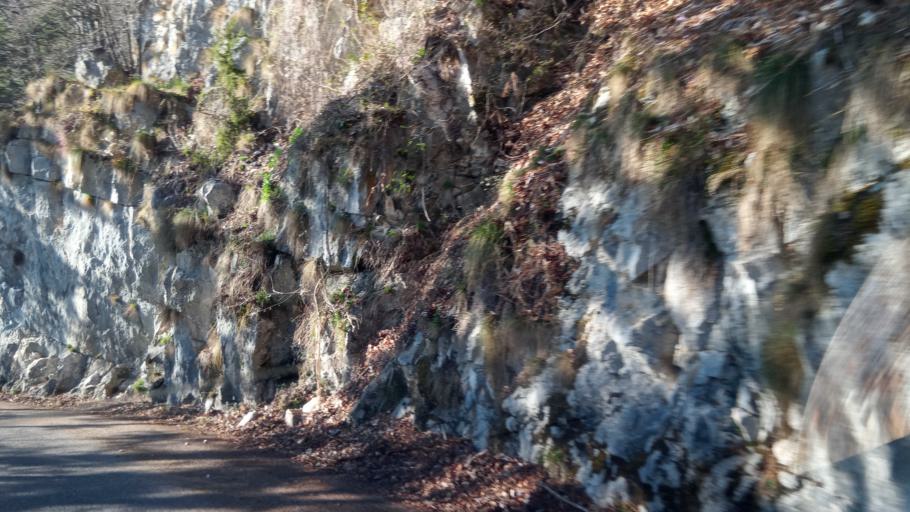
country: IT
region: Veneto
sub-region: Provincia di Treviso
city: Borso del Grappa
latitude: 45.8324
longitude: 11.7788
